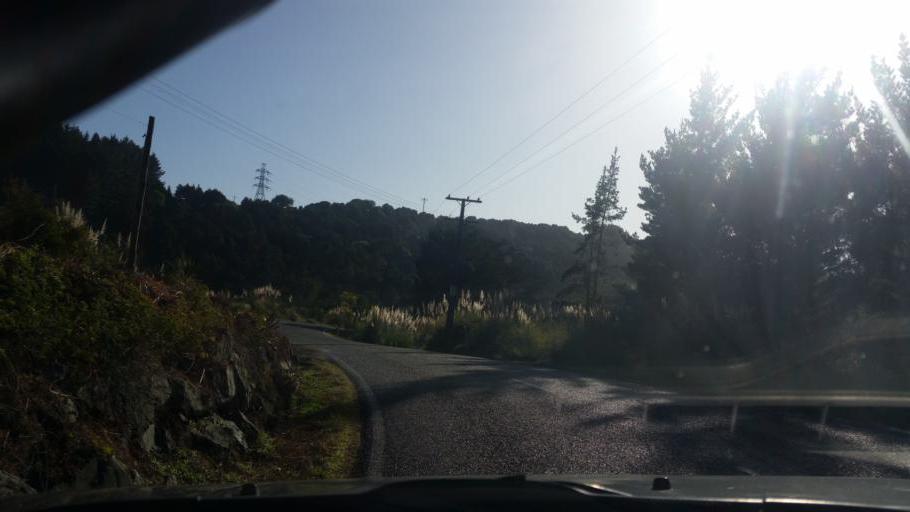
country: NZ
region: Auckland
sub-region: Auckland
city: Wellsford
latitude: -36.2153
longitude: 174.4680
